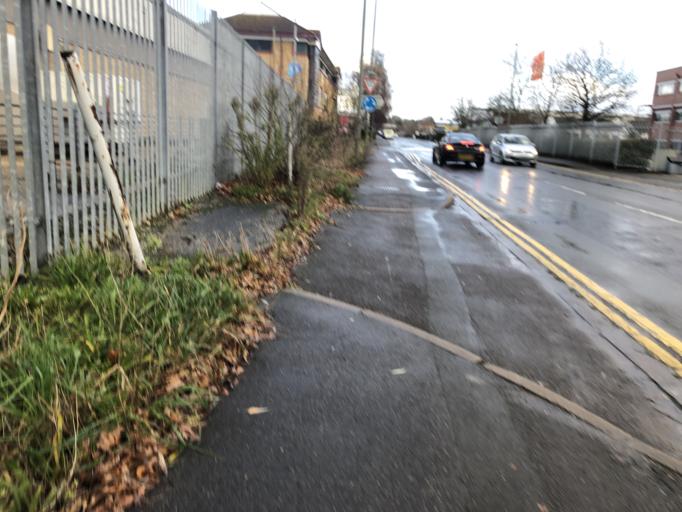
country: GB
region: England
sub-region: Bracknell Forest
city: Sandhurst
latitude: 51.3316
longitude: -0.7698
